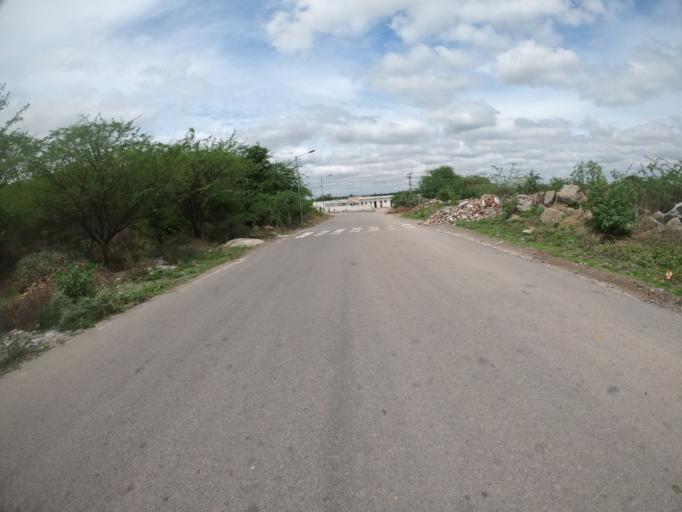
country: IN
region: Telangana
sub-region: Hyderabad
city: Hyderabad
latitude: 17.2994
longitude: 78.3787
